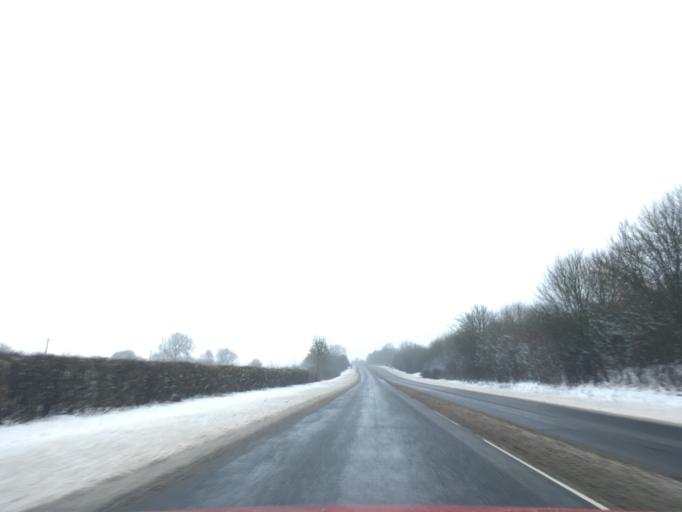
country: GB
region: England
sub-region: Warwickshire
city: Stratford-upon-Avon
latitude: 52.2042
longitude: -1.7370
